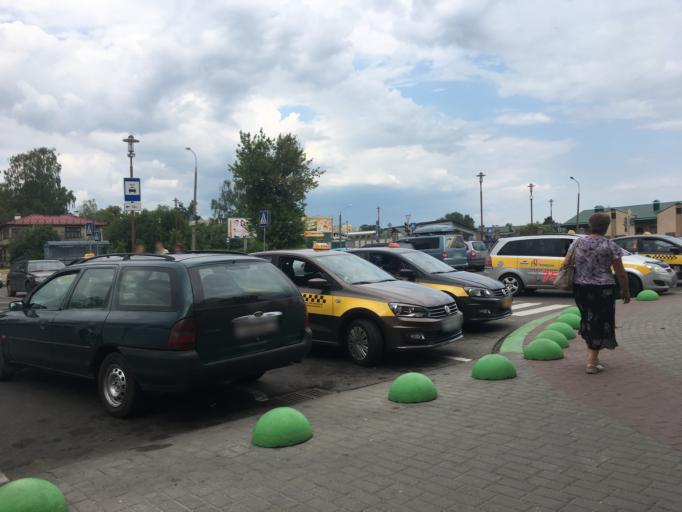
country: BY
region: Grodnenskaya
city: Hrodna
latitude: 53.6890
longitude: 23.8456
